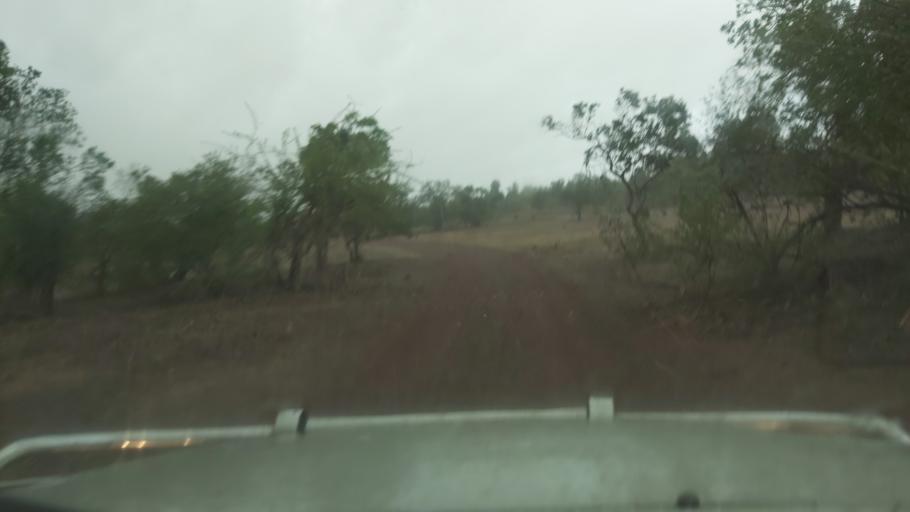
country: ML
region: Koulikoro
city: Banamba
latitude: 13.3659
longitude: -7.1203
